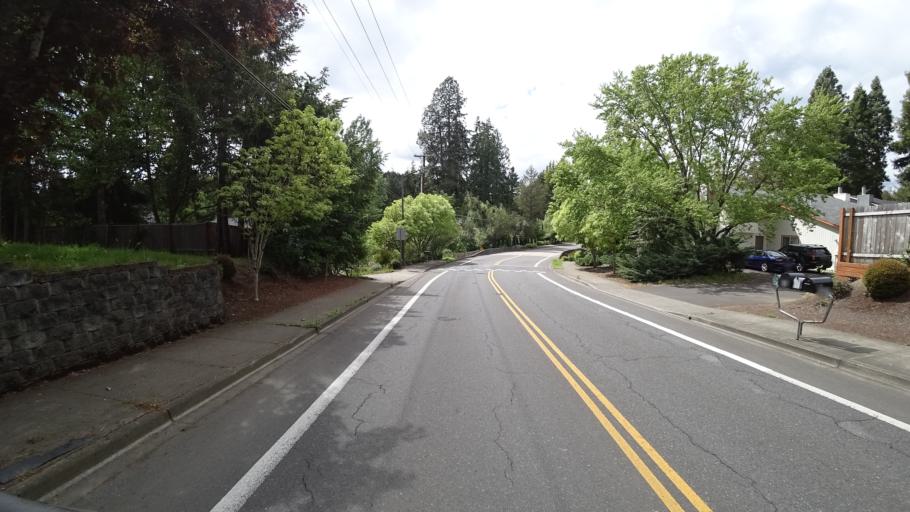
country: US
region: Oregon
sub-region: Washington County
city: Beaverton
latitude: 45.4746
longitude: -122.8317
